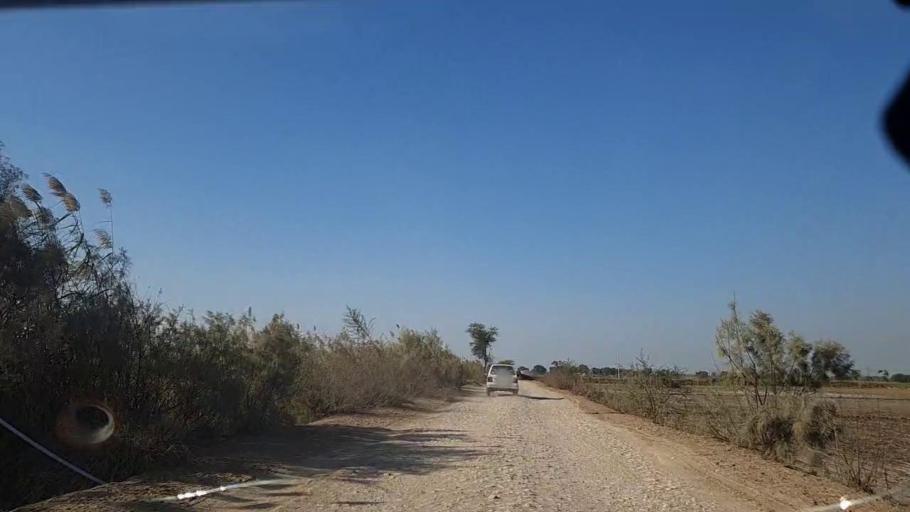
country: PK
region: Sindh
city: Khanpur
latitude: 27.7823
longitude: 69.3550
